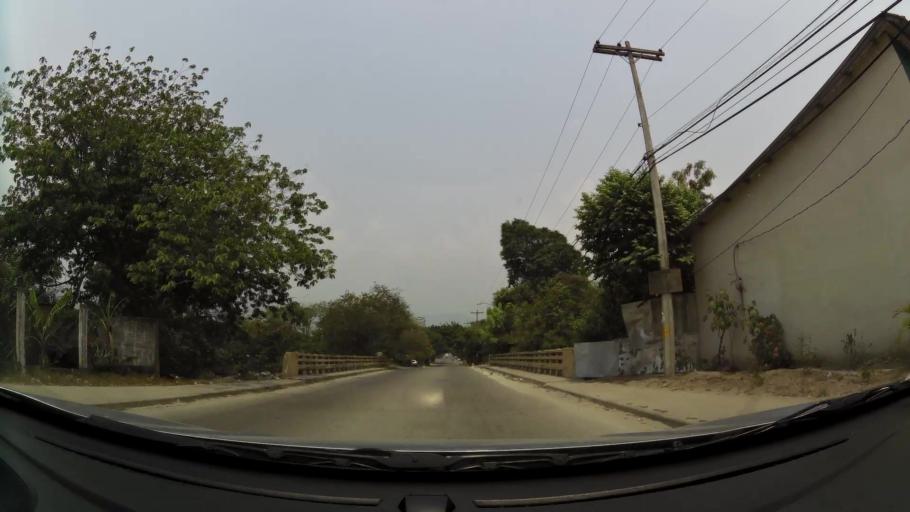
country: HN
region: Cortes
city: San Pedro Sula
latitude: 15.4849
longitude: -88.0088
